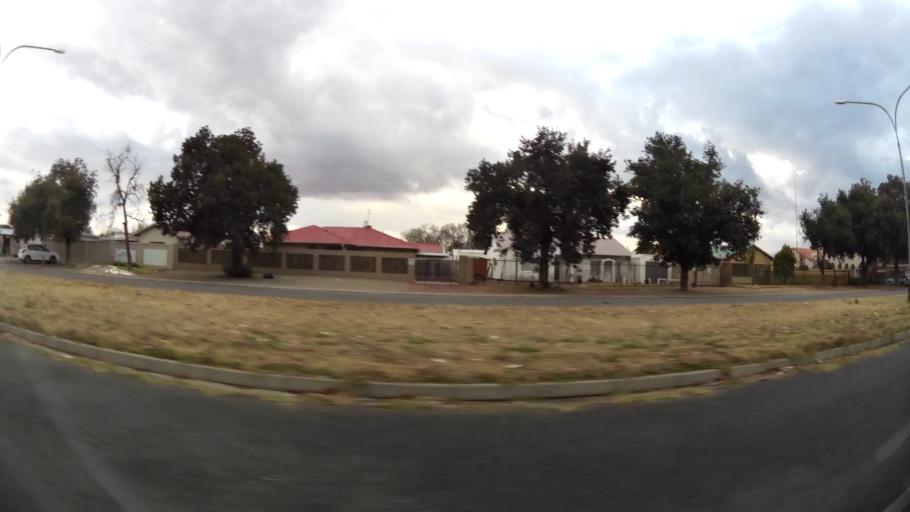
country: ZA
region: Orange Free State
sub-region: Lejweleputswa District Municipality
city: Welkom
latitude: -27.9686
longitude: 26.7461
